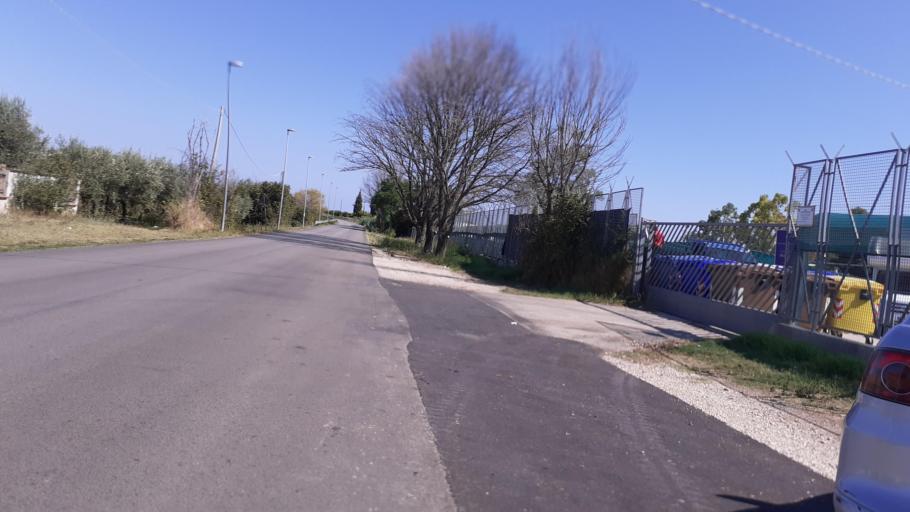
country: IT
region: Abruzzo
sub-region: Provincia di Chieti
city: Vasto
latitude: 42.1550
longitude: 14.7160
